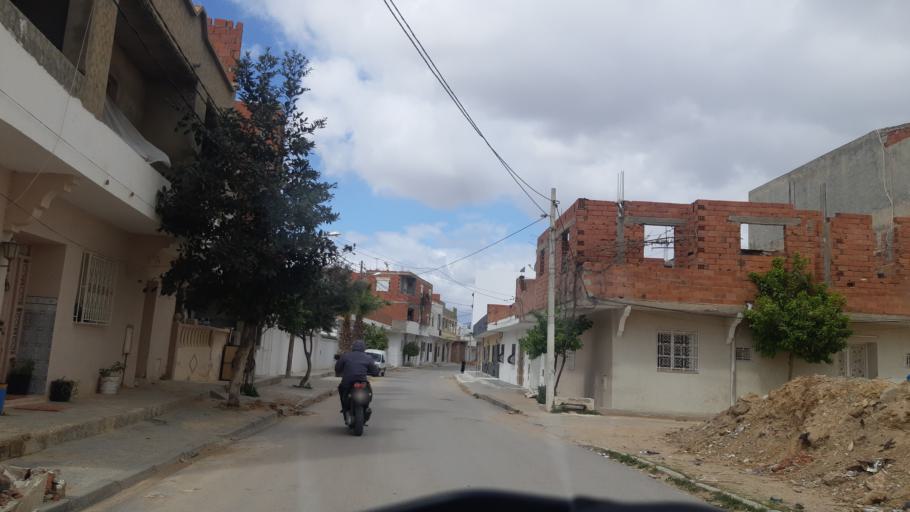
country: TN
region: Susah
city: Akouda
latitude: 35.8645
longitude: 10.5378
